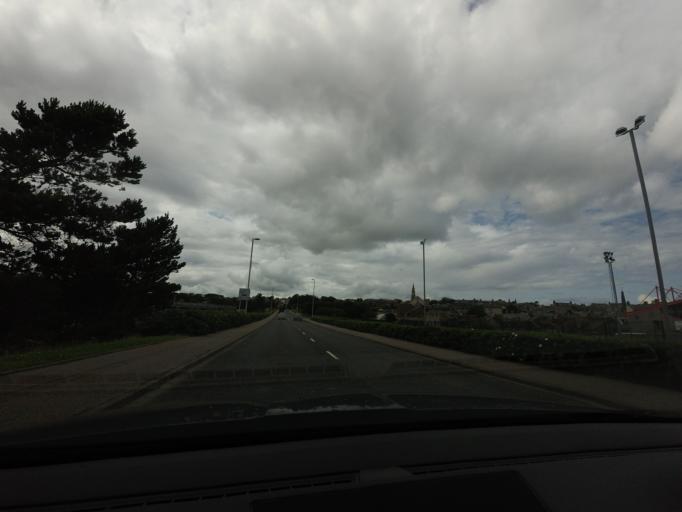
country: GB
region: Scotland
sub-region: Aberdeenshire
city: Banff
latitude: 57.6624
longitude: -2.5174
